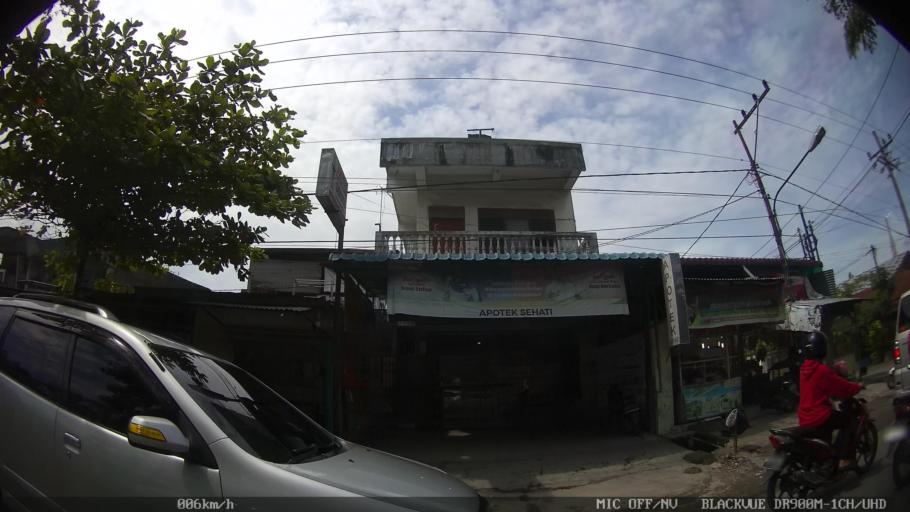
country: ID
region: North Sumatra
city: Medan
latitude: 3.5872
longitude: 98.7188
